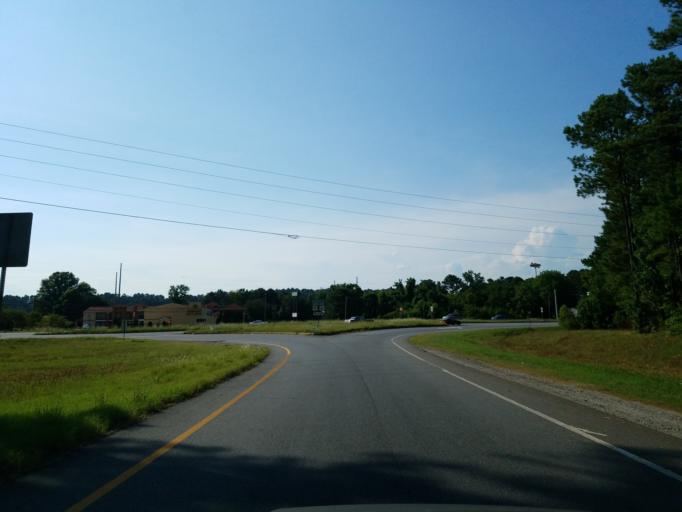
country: US
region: Georgia
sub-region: Bartow County
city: Cartersville
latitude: 34.2469
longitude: -84.7716
